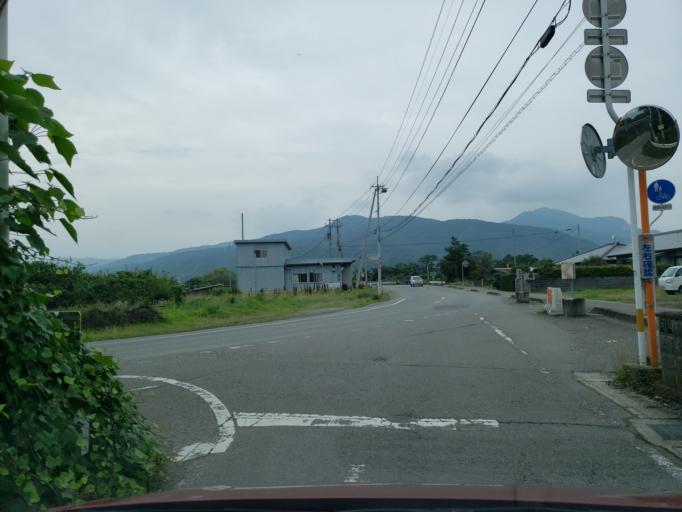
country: JP
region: Tokushima
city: Kamojimacho-jogejima
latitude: 34.1018
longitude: 134.2780
